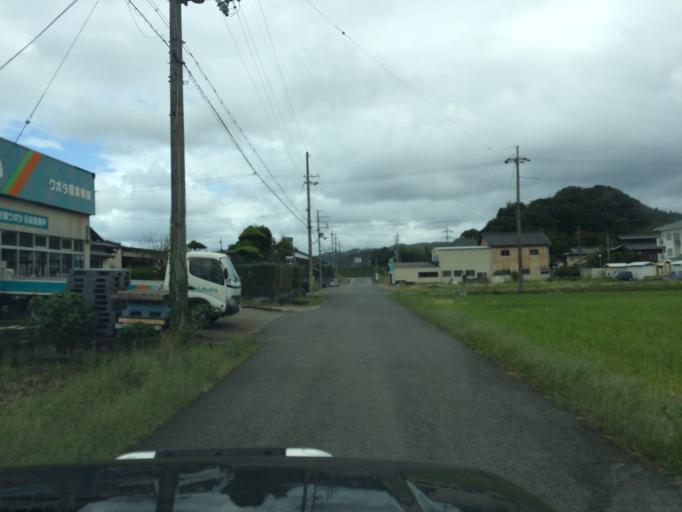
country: JP
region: Hyogo
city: Toyooka
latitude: 35.4773
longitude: 134.7838
